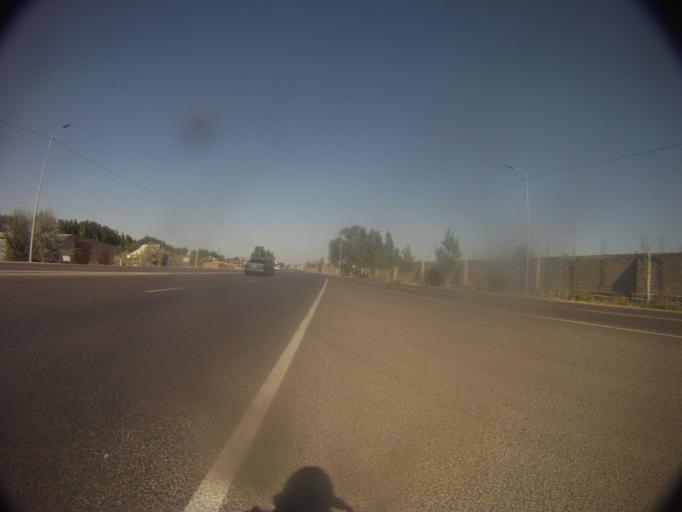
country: KZ
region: Zhambyl
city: Taraz
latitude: 42.9222
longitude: 71.4043
